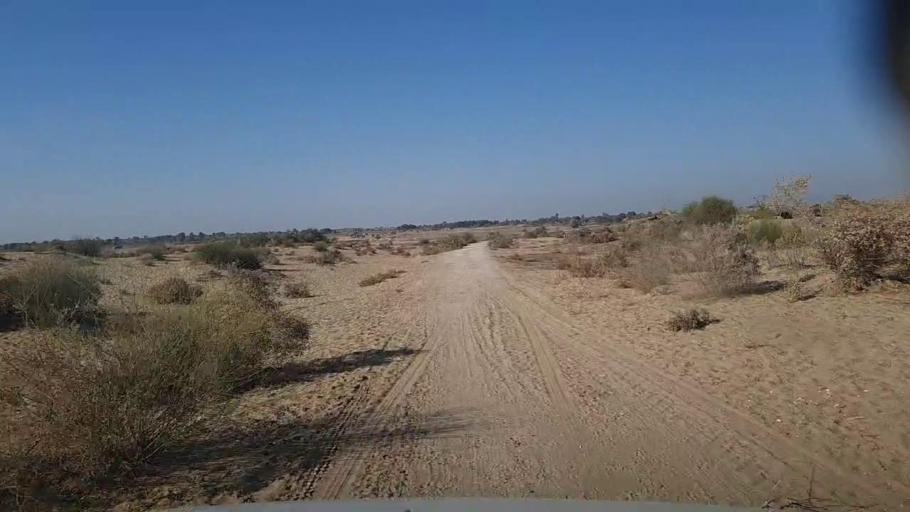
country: PK
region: Sindh
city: Khairpur
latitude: 27.9620
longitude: 69.8117
